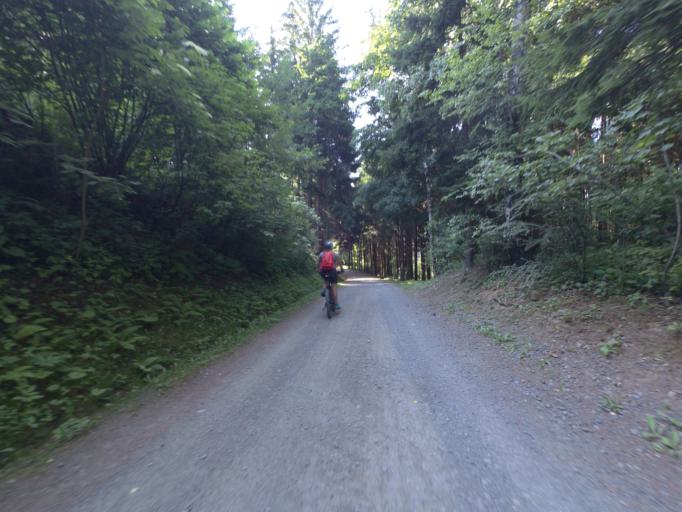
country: AT
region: Carinthia
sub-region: Politischer Bezirk Spittal an der Drau
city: Seeboden
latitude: 46.8082
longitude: 13.5229
